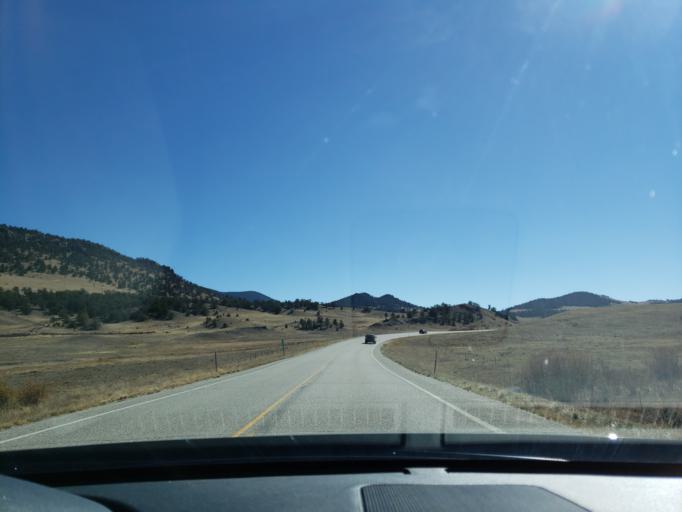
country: US
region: Colorado
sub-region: Chaffee County
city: Salida
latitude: 38.8600
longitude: -105.6556
